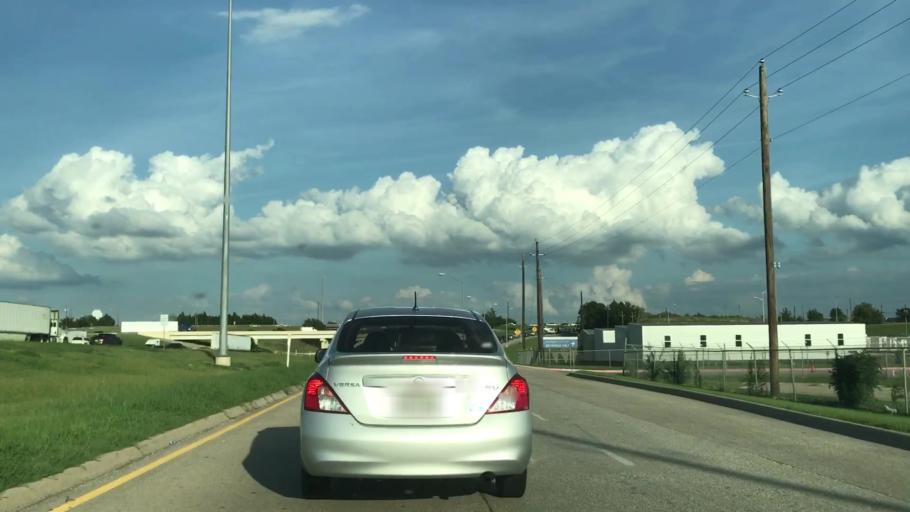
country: US
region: Texas
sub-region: Dallas County
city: Cockrell Hill
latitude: 32.7665
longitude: -96.8611
